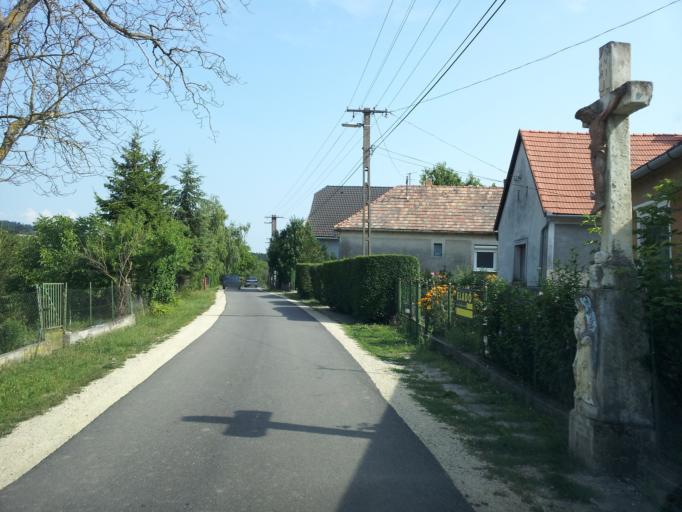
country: HU
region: Veszprem
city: Balatonfured
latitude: 47.0017
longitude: 17.8267
